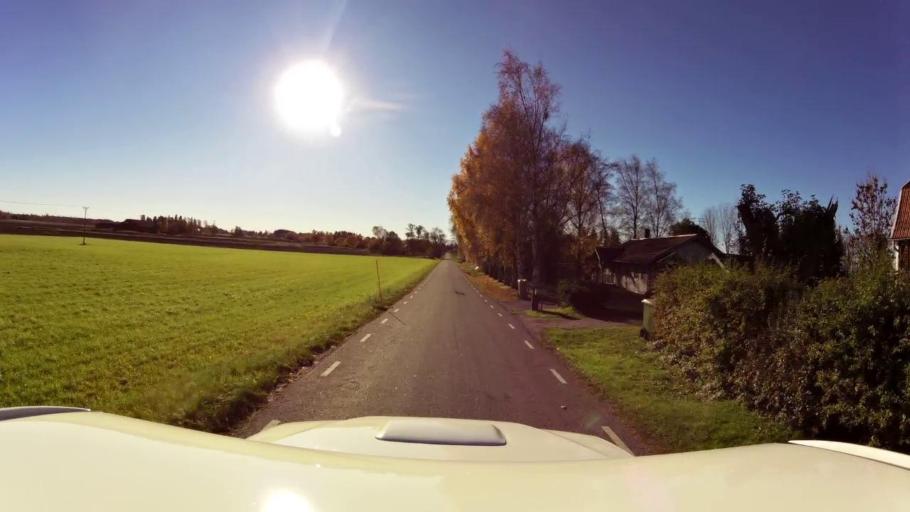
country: SE
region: OEstergoetland
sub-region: Linkopings Kommun
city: Ljungsbro
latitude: 58.4997
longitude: 15.4187
